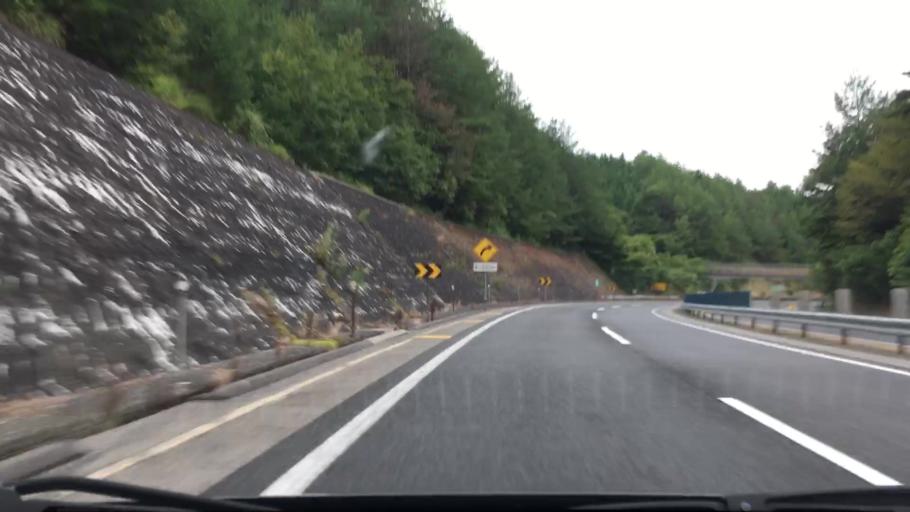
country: JP
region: Hiroshima
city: Miyoshi
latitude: 34.6916
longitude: 132.5908
